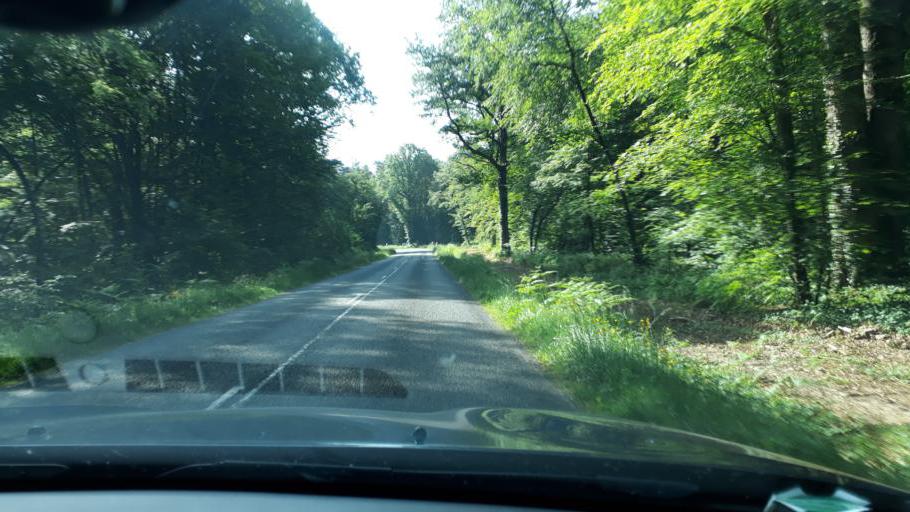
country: FR
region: Centre
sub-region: Departement du Loiret
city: Chilleurs-aux-Bois
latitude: 48.0630
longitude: 2.2296
